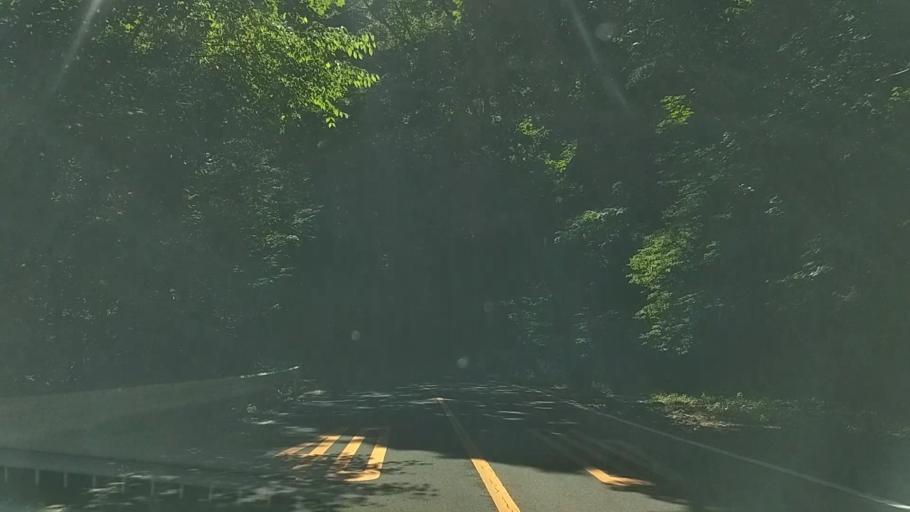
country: JP
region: Nagano
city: Saku
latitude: 36.3527
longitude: 138.6578
